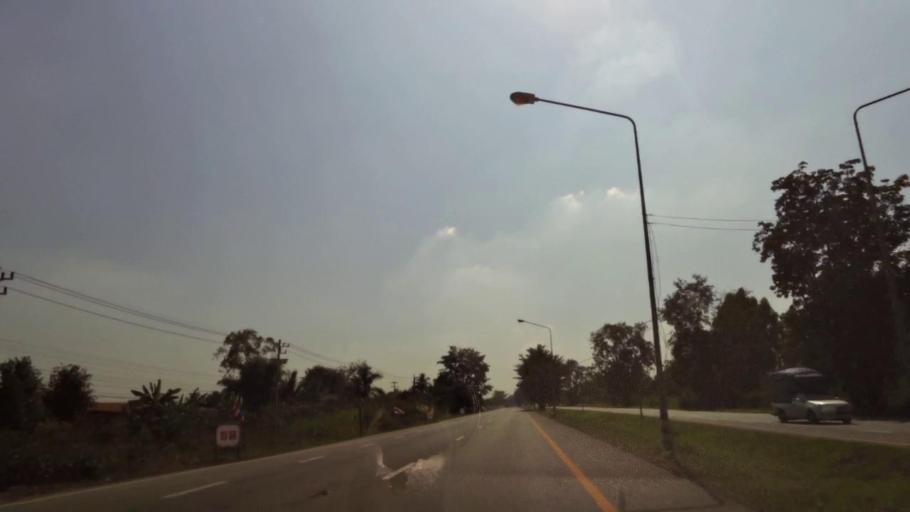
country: TH
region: Phichit
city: Bueng Na Rang
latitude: 16.2416
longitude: 100.1254
